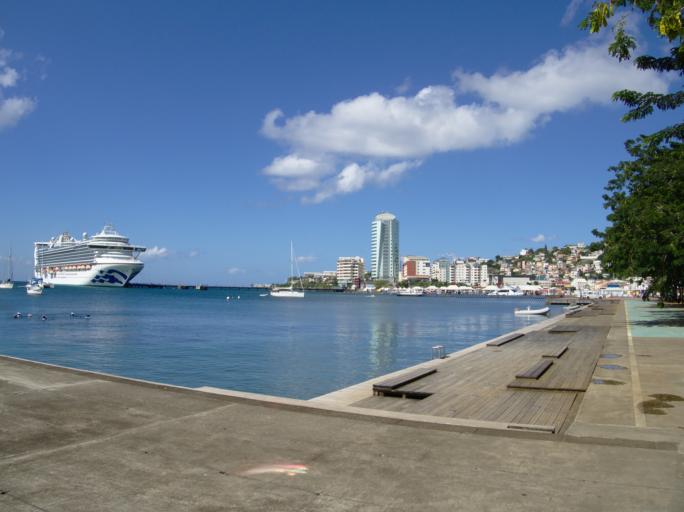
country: MQ
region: Martinique
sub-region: Martinique
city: Fort-de-France
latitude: 14.6015
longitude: -61.0679
